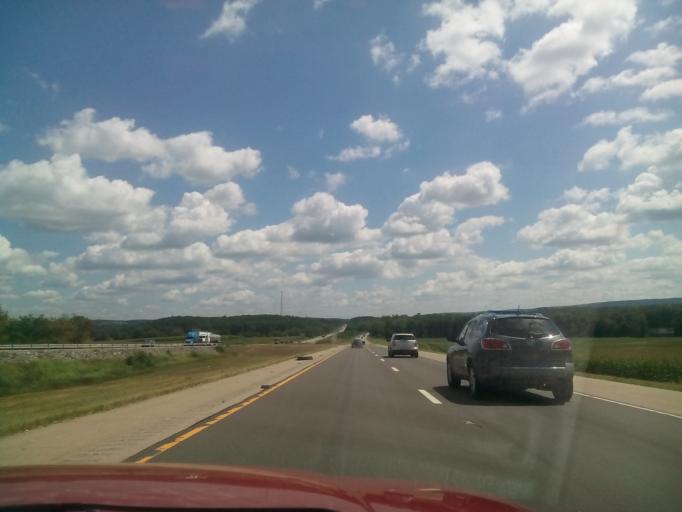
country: US
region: Pennsylvania
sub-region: Northumberland County
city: Milton
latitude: 41.0091
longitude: -76.7738
